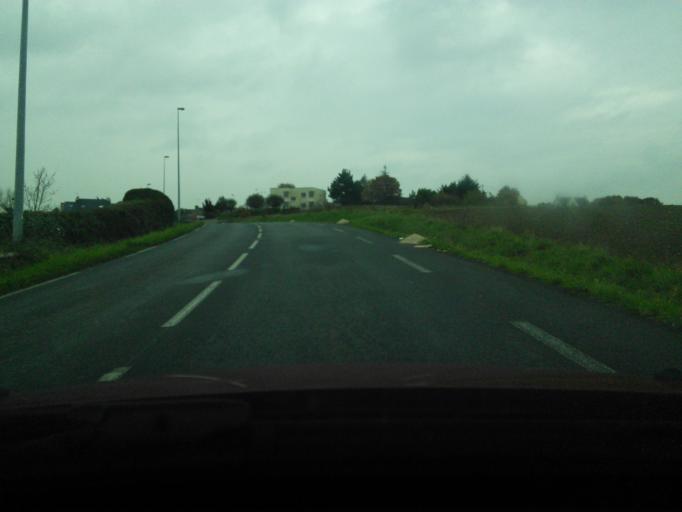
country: FR
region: Brittany
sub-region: Departement des Cotes-d'Armor
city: Yffiniac
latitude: 48.4797
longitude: -2.6865
